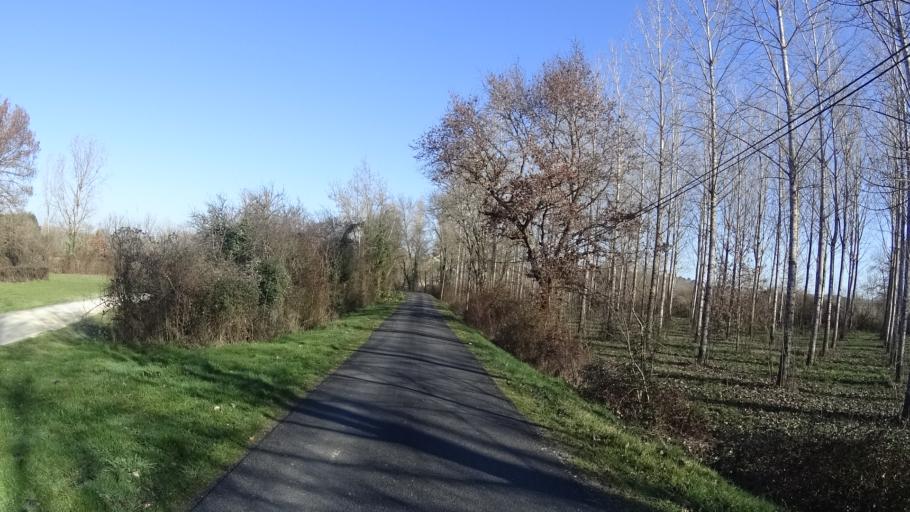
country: FR
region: Aquitaine
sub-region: Departement de la Dordogne
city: Montpon-Menesterol
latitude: 45.0275
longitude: 0.2256
